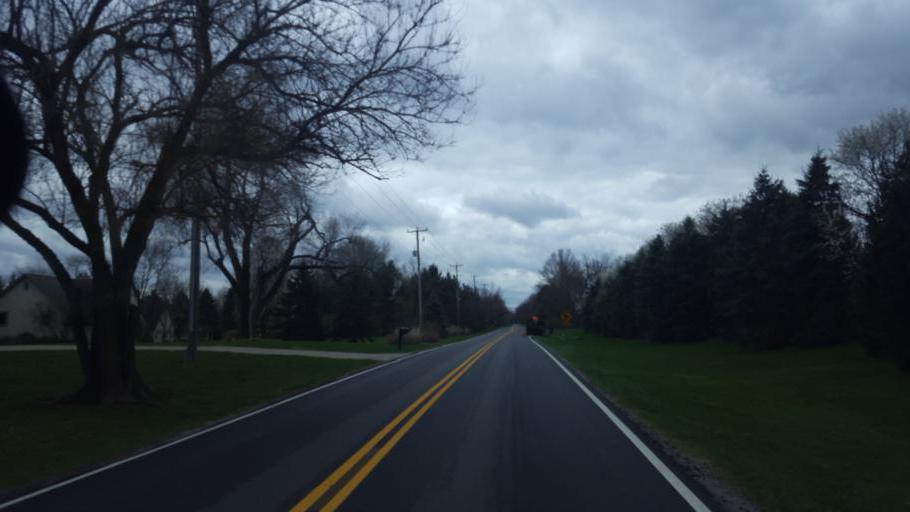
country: US
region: Ohio
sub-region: Franklin County
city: Westerville
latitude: 40.1569
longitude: -82.8799
